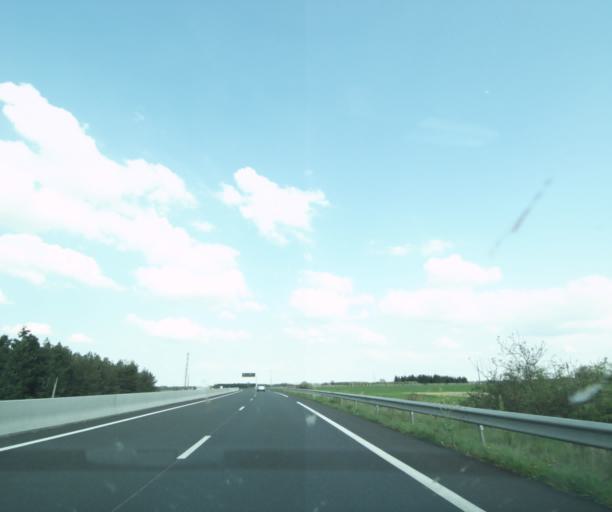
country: FR
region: Auvergne
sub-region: Departement de l'Allier
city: Bessay-sur-Allier
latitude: 46.4592
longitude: 3.2745
